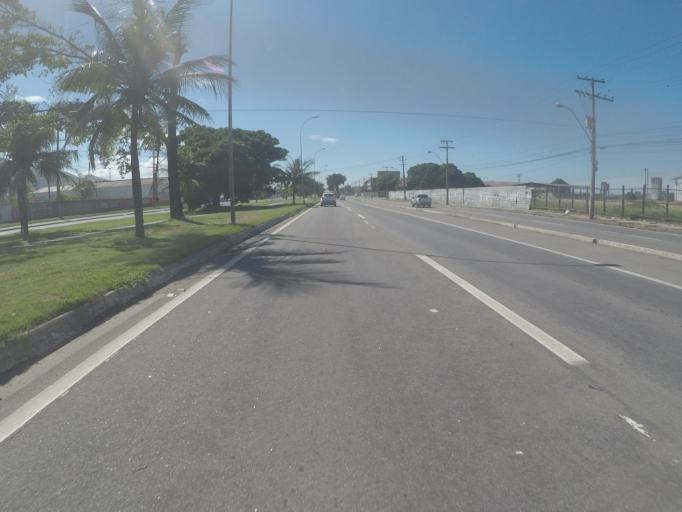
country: BR
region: Espirito Santo
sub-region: Serra
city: Serra
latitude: -20.2114
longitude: -40.2696
